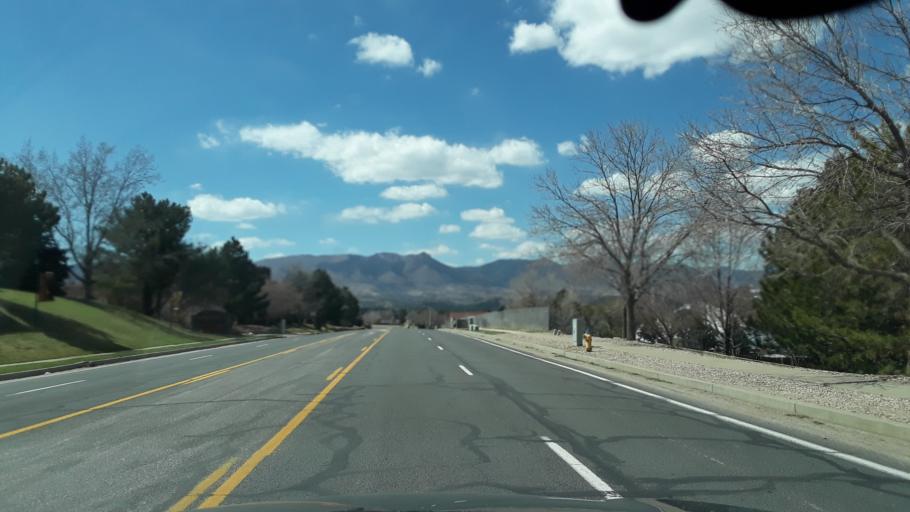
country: US
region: Colorado
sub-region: El Paso County
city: Colorado Springs
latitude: 38.9145
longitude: -104.7779
